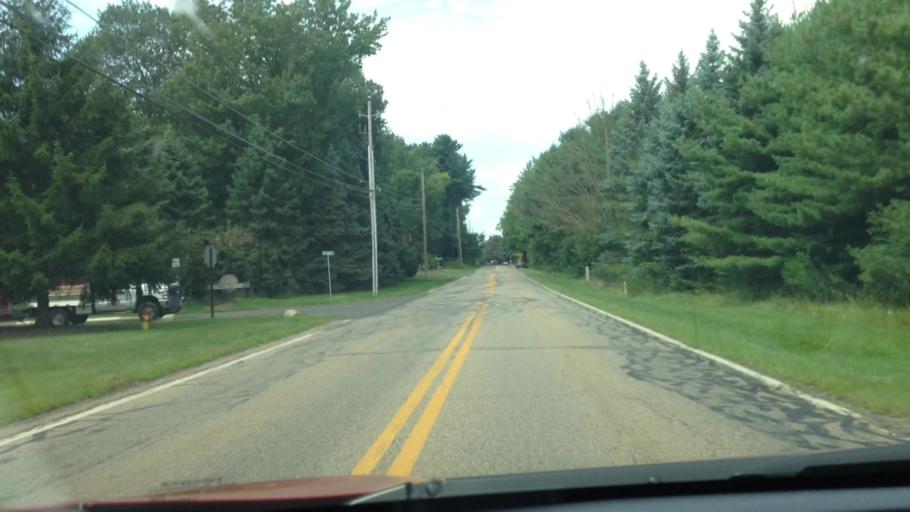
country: US
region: Ohio
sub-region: Stark County
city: Perry Heights
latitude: 40.8262
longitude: -81.4691
